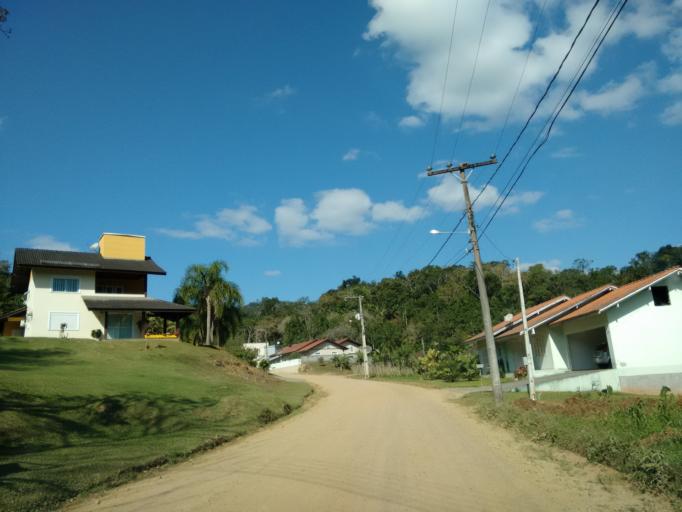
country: BR
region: Santa Catarina
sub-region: Pomerode
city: Pomerode
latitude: -26.7391
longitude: -49.1631
